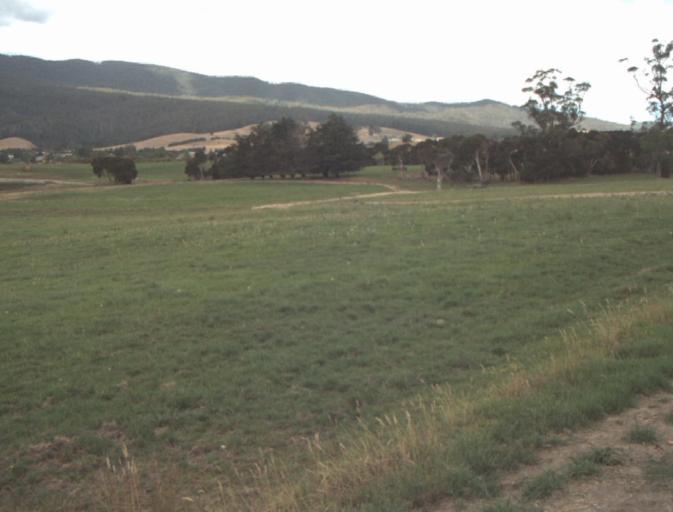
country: AU
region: Tasmania
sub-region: Launceston
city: Mayfield
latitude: -41.2380
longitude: 147.2066
